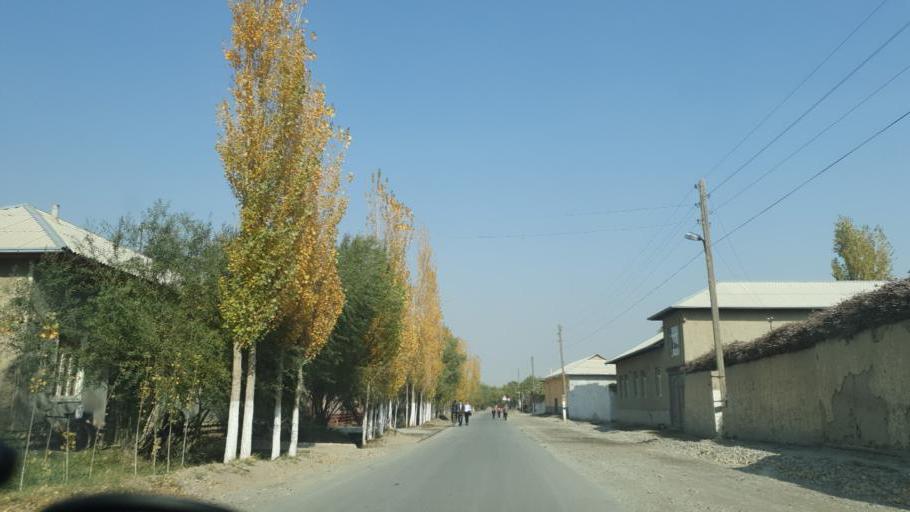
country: UZ
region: Fergana
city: Beshariq
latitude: 40.4930
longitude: 70.6212
